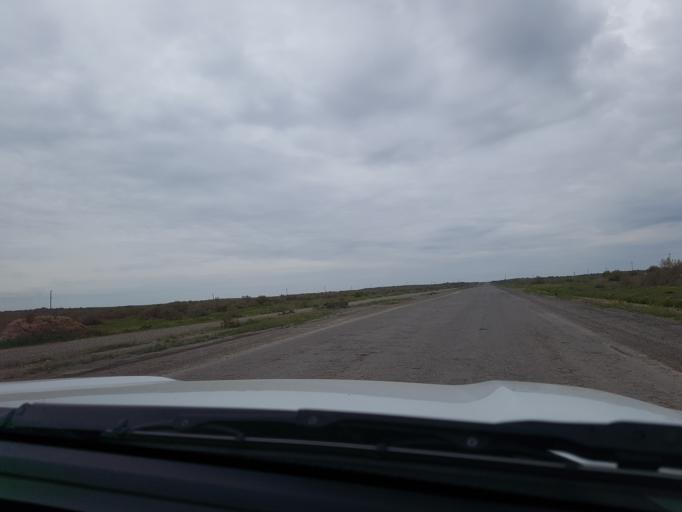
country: TM
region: Mary
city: Bayramaly
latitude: 37.9236
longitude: 62.6244
